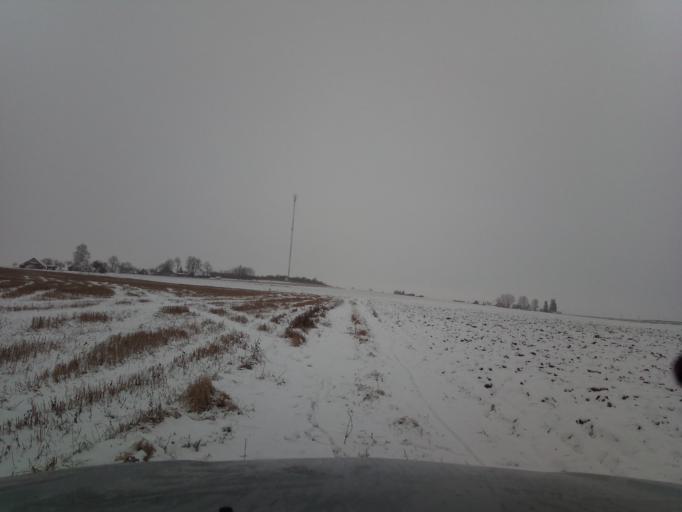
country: LT
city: Ramygala
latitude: 55.4841
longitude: 24.2929
